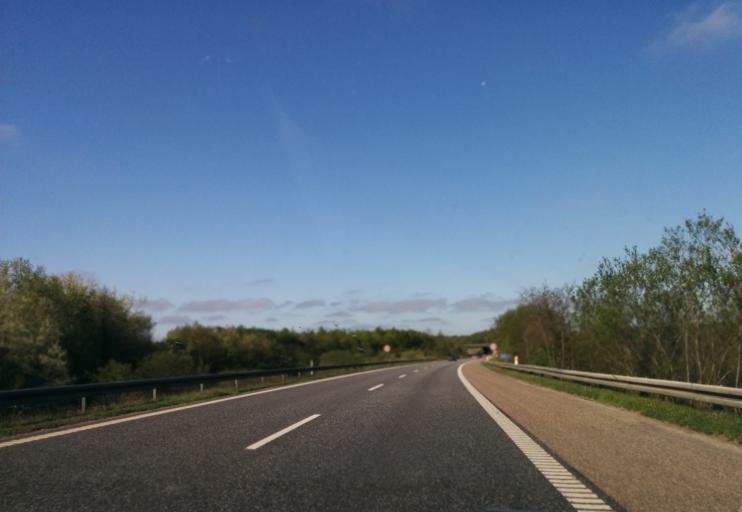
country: DK
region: Central Jutland
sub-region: Skanderborg Kommune
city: Horning
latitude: 56.1044
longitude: 10.0435
